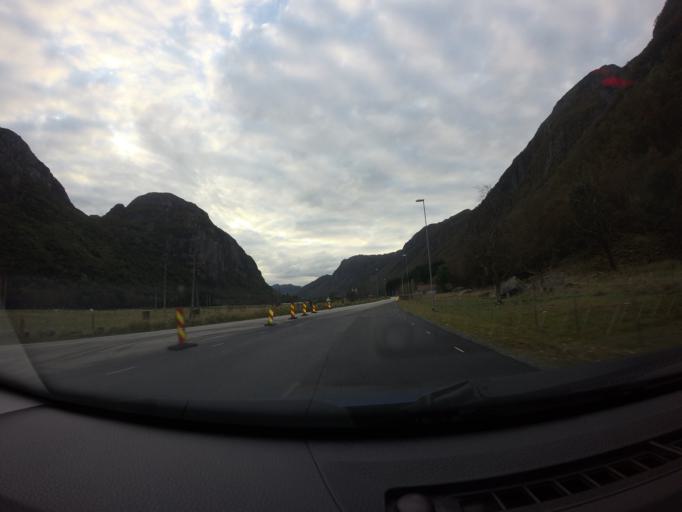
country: NO
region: Rogaland
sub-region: Forsand
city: Forsand
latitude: 58.8299
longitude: 6.1854
